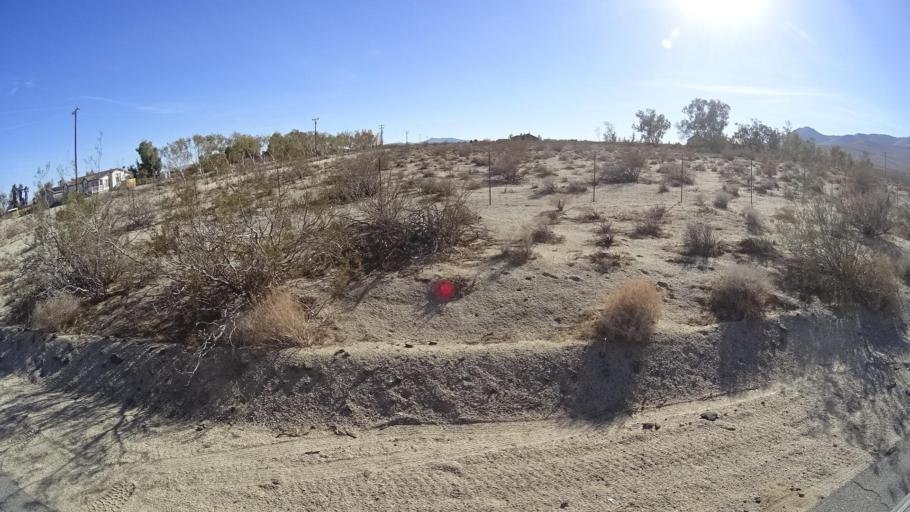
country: US
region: California
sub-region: Kern County
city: Inyokern
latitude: 35.6812
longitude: -117.8553
